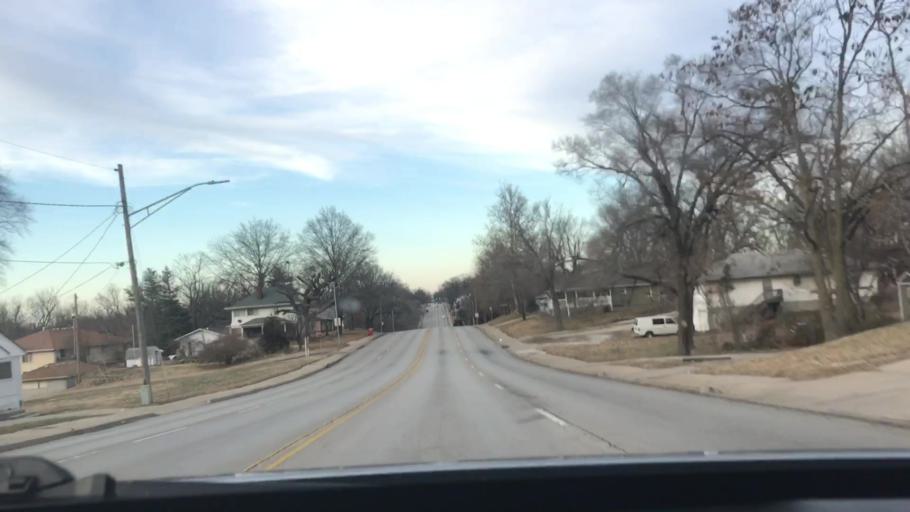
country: US
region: Missouri
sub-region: Jackson County
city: Independence
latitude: 39.0717
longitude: -94.4464
